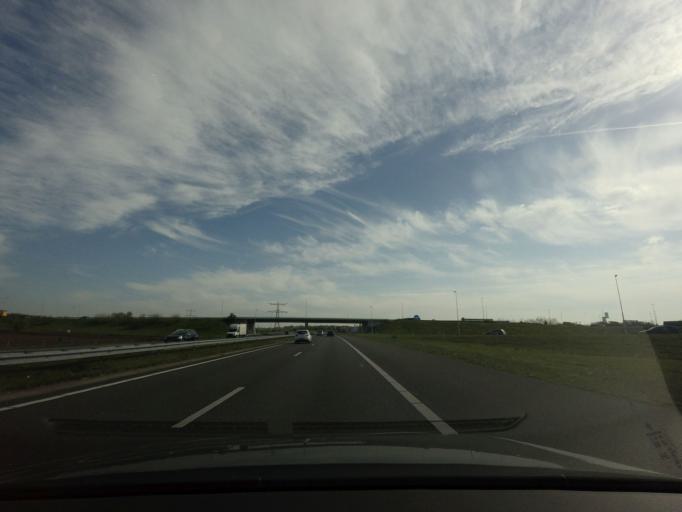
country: NL
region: North Brabant
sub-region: Gemeente Bernheze
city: Heesch
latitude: 51.7164
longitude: 5.5683
